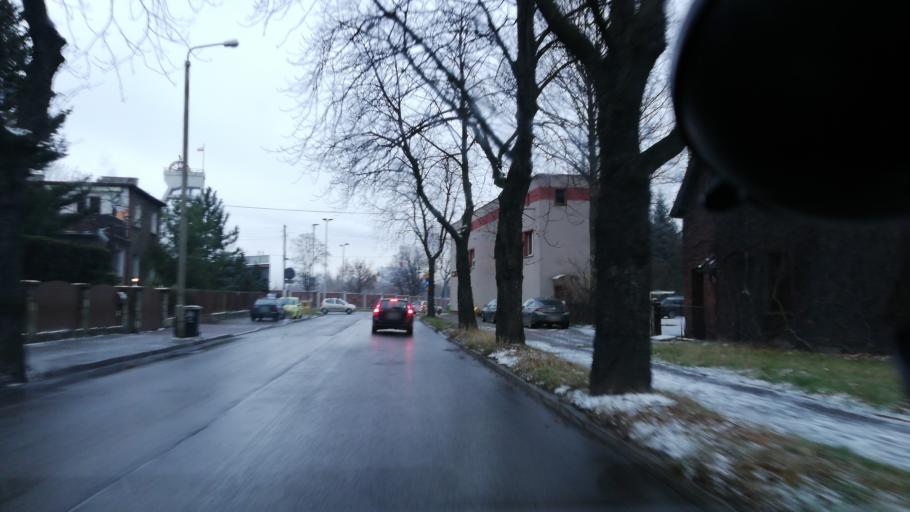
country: PL
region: Silesian Voivodeship
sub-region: Chorzow
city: Chorzow
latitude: 50.2961
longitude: 18.9677
